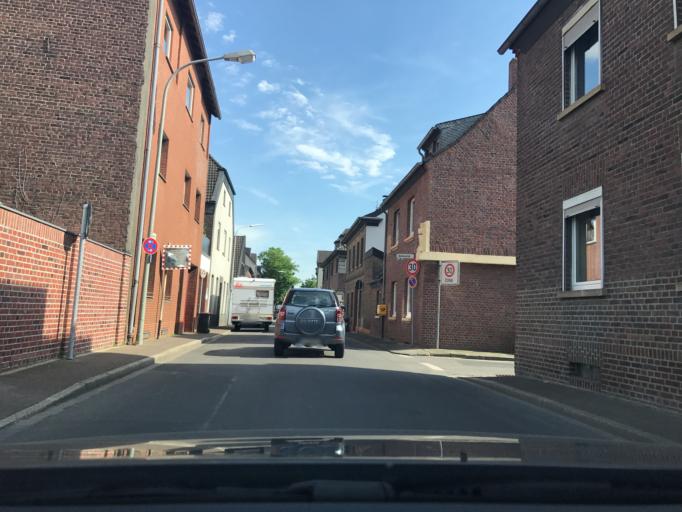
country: DE
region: North Rhine-Westphalia
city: Tonisvorst
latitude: 51.3700
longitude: 6.5111
